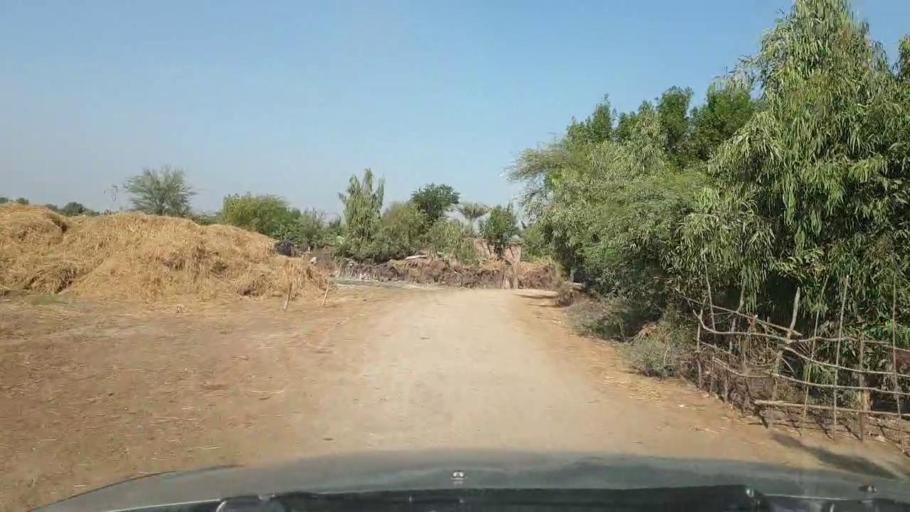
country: PK
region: Sindh
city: Tando Muhammad Khan
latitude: 25.1407
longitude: 68.5355
